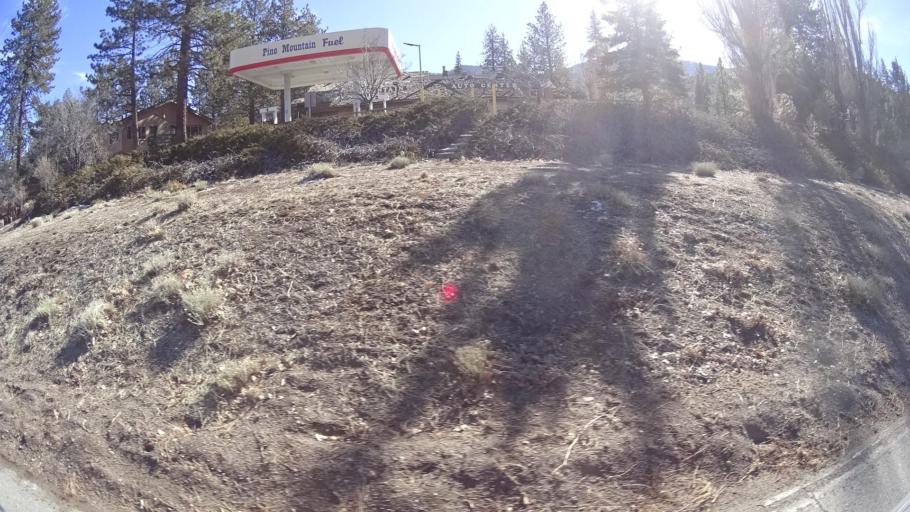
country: US
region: California
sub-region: Kern County
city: Pine Mountain Club
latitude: 34.8510
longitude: -119.1665
